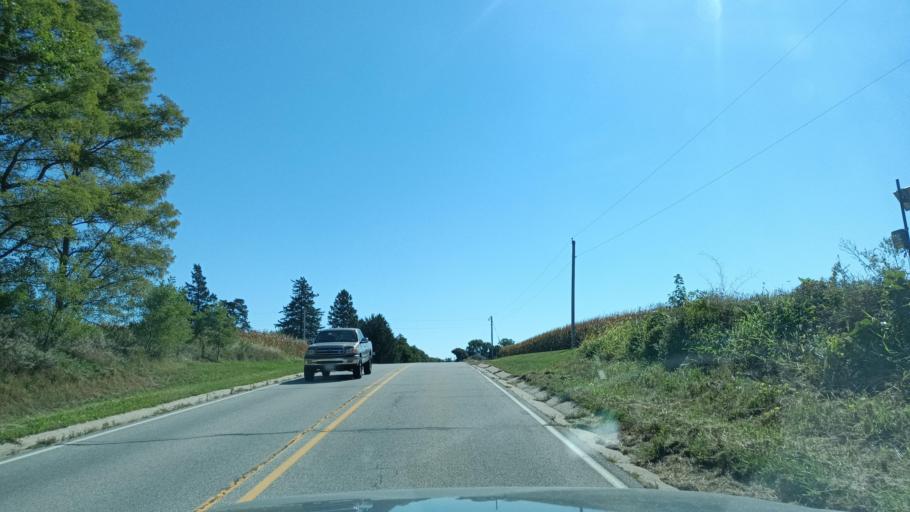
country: US
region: Illinois
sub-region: Peoria County
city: Elmwood
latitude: 40.8435
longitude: -89.9001
